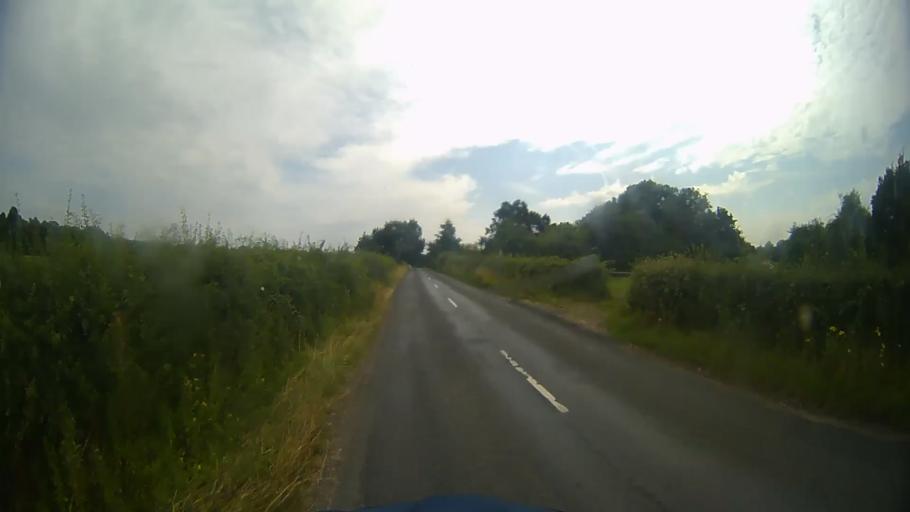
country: GB
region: England
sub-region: Hampshire
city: Kingsley
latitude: 51.1658
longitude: -0.8573
